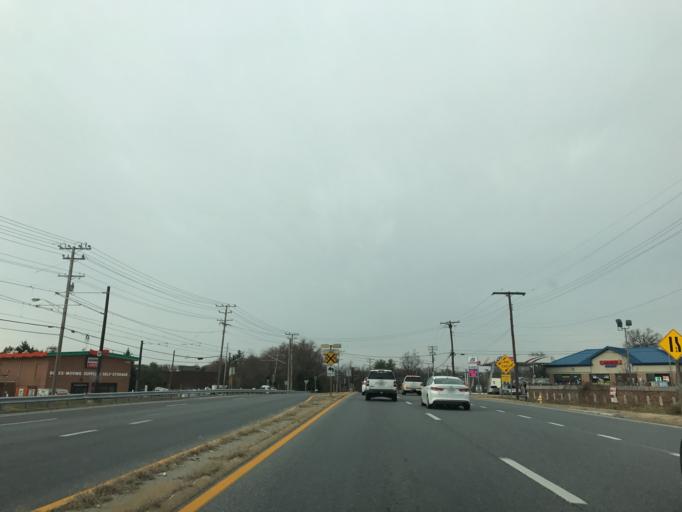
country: US
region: Maryland
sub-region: Anne Arundel County
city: Ferndale
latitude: 39.1775
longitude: -76.6372
